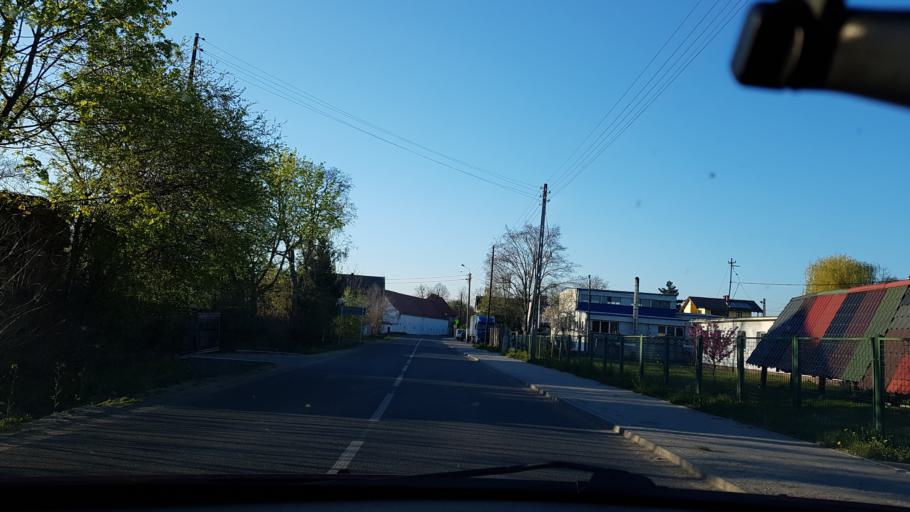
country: PL
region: Opole Voivodeship
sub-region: Powiat nyski
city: Nysa
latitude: 50.4298
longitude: 17.3059
